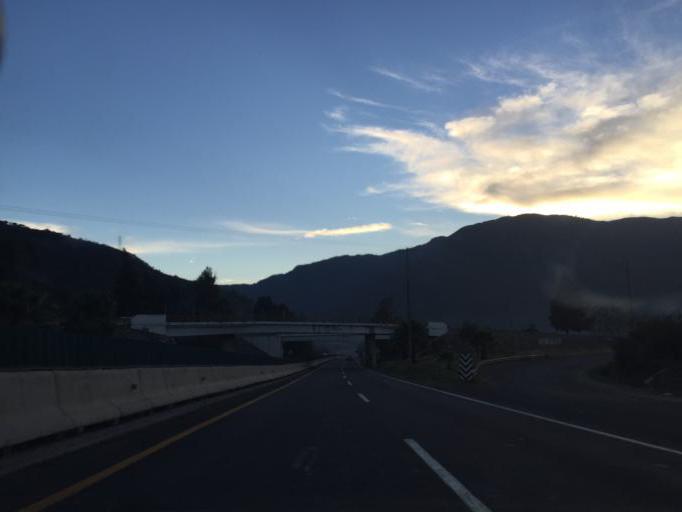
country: MX
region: Veracruz
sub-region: Nogales
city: Agricola Lazaro Cardenas
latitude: 18.8138
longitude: -97.1914
